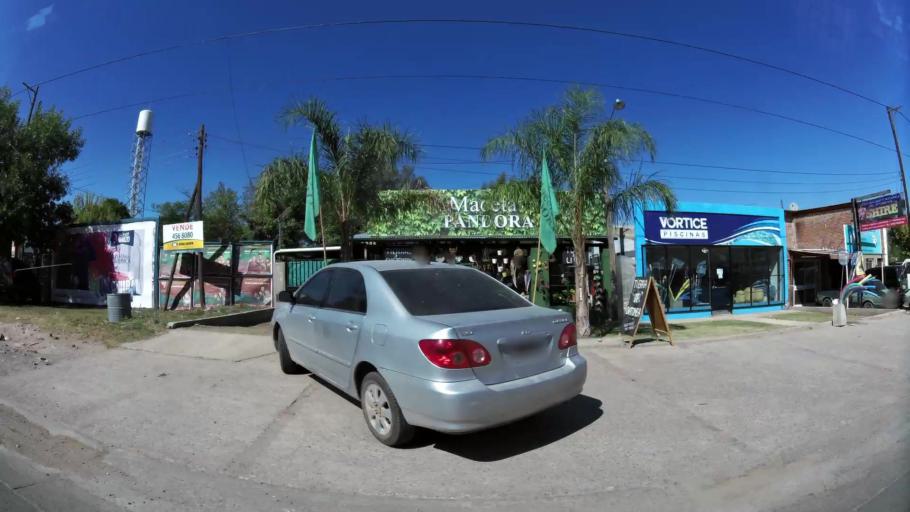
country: AR
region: Cordoba
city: Villa Allende
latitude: -31.3156
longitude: -64.2882
